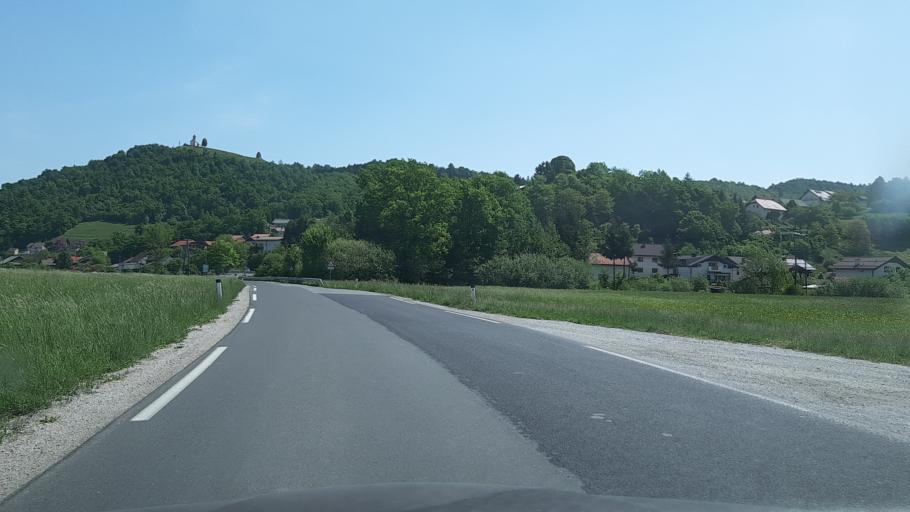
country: SI
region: Brezovica
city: Notranje Gorice
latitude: 45.9660
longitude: 14.4081
